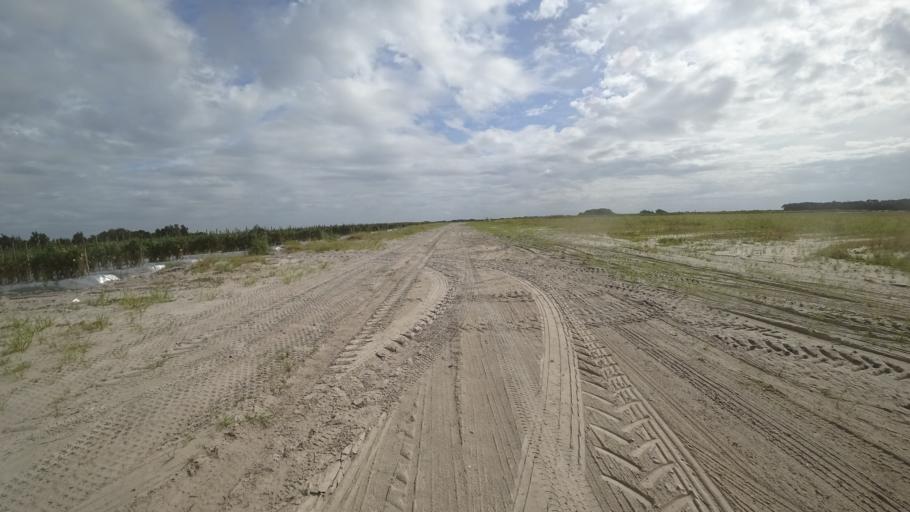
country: US
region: Florida
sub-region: Hillsborough County
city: Wimauma
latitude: 27.5830
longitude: -82.3208
